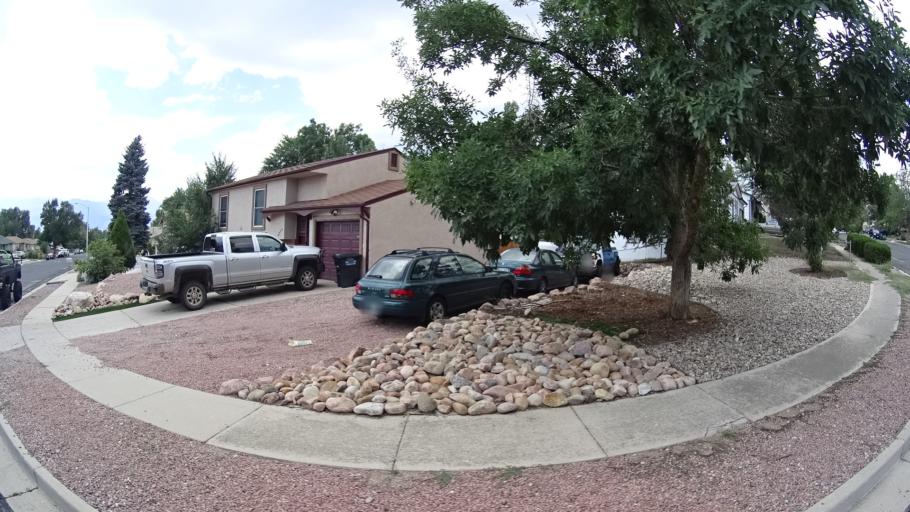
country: US
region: Colorado
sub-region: El Paso County
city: Cimarron Hills
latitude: 38.8295
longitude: -104.7393
